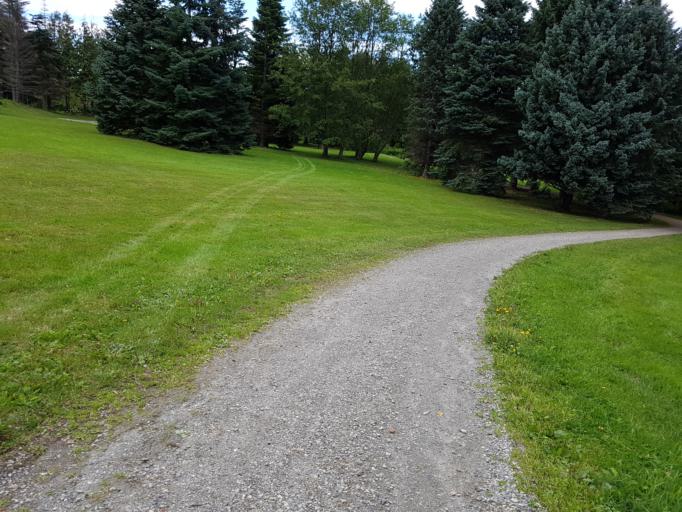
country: NO
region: Sor-Trondelag
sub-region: Trondheim
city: Trondheim
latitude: 63.4480
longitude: 10.4518
